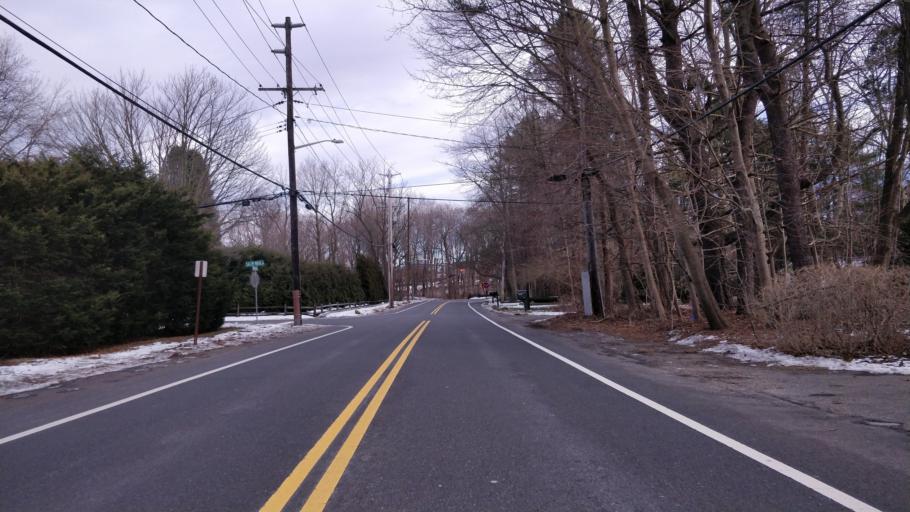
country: US
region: New York
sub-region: Suffolk County
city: Centerport
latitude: 40.8719
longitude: -73.3853
